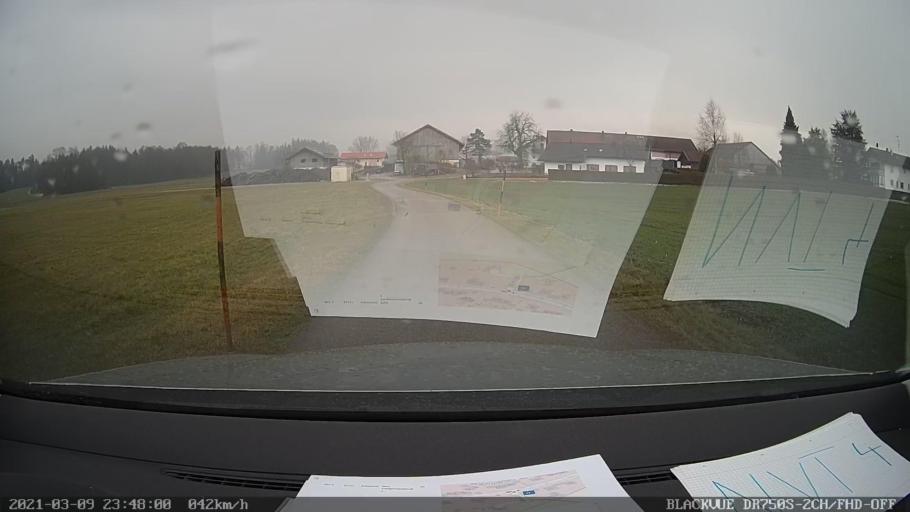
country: DE
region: Bavaria
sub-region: Upper Bavaria
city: Schonstett
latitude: 47.9810
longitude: 12.2570
